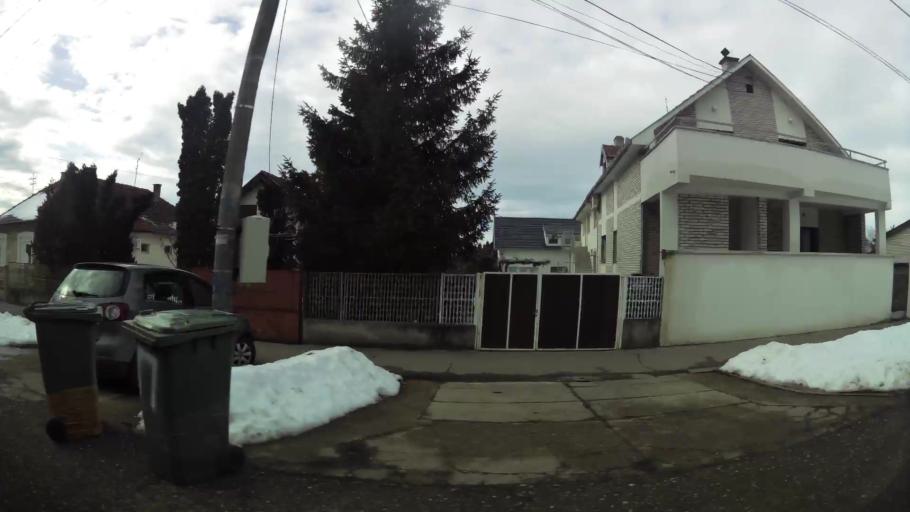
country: RS
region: Central Serbia
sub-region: Belgrade
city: Surcin
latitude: 44.7948
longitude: 20.2784
